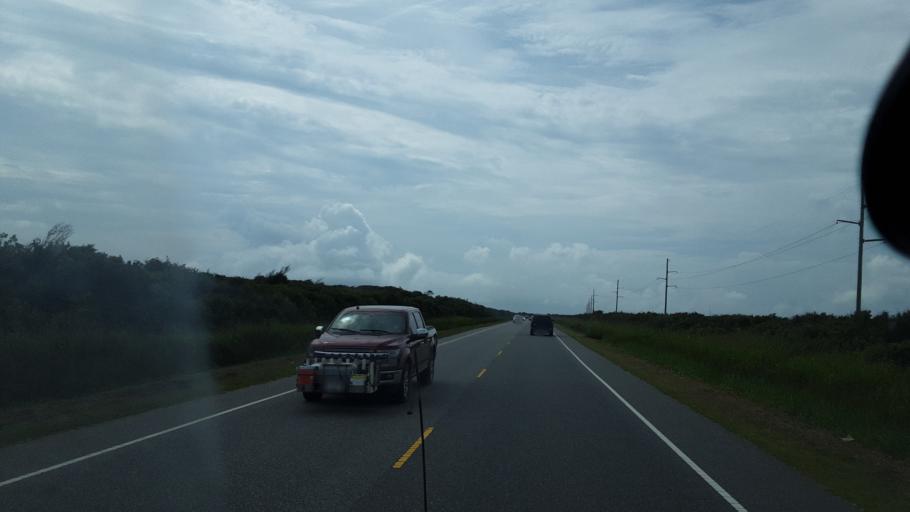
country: US
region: North Carolina
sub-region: Dare County
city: Wanchese
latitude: 35.8246
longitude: -75.5558
